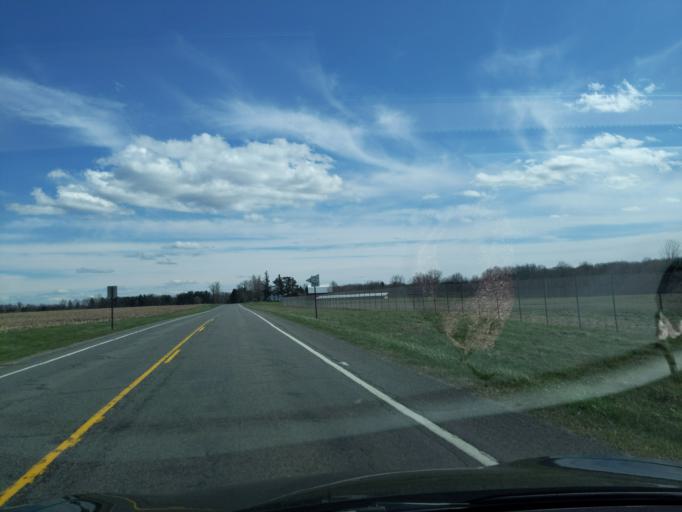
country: US
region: Michigan
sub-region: Ingham County
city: Mason
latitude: 42.5664
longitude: -84.4131
